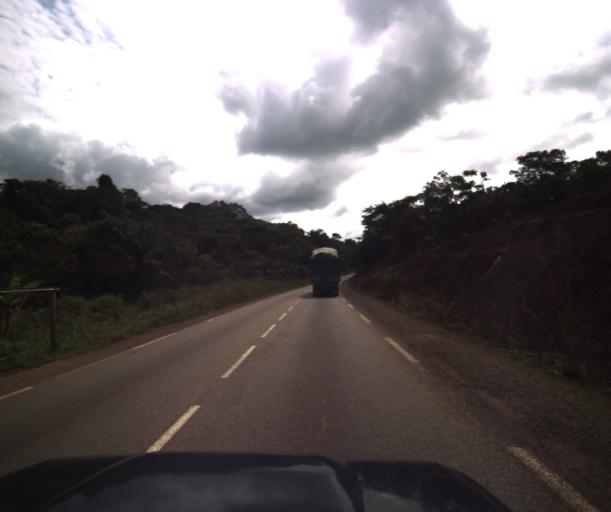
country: CM
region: Littoral
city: Edea
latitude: 3.8147
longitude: 10.3314
